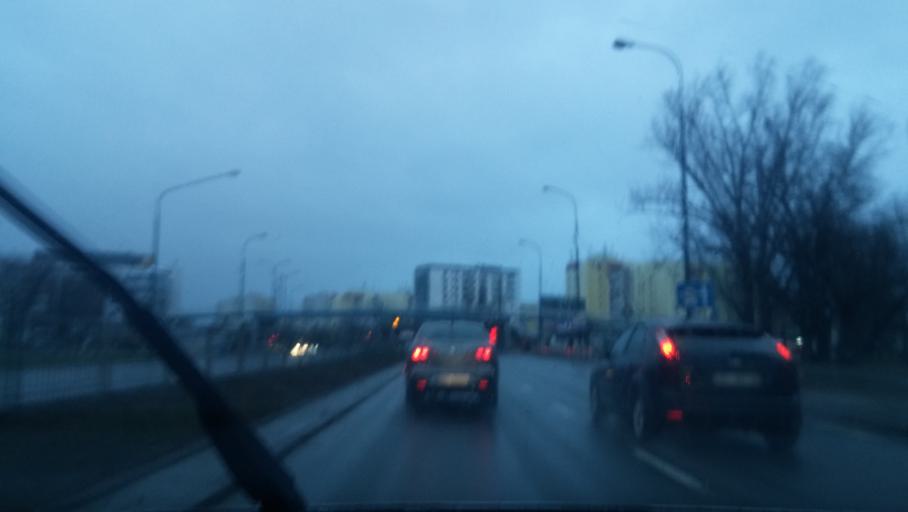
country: PL
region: Masovian Voivodeship
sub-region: Warszawa
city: Praga Poludnie
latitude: 52.2359
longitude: 21.0897
